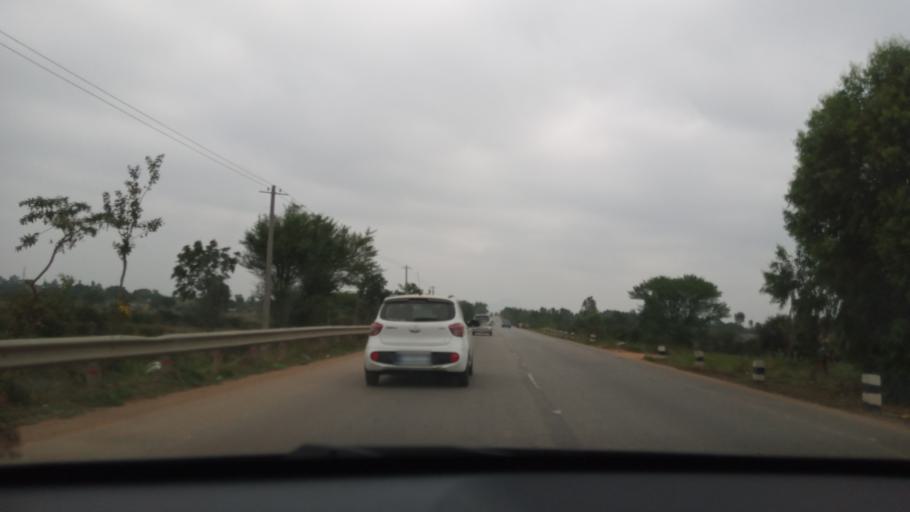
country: IN
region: Karnataka
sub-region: Bangalore Rural
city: Vijayapura
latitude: 13.2656
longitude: 77.9465
